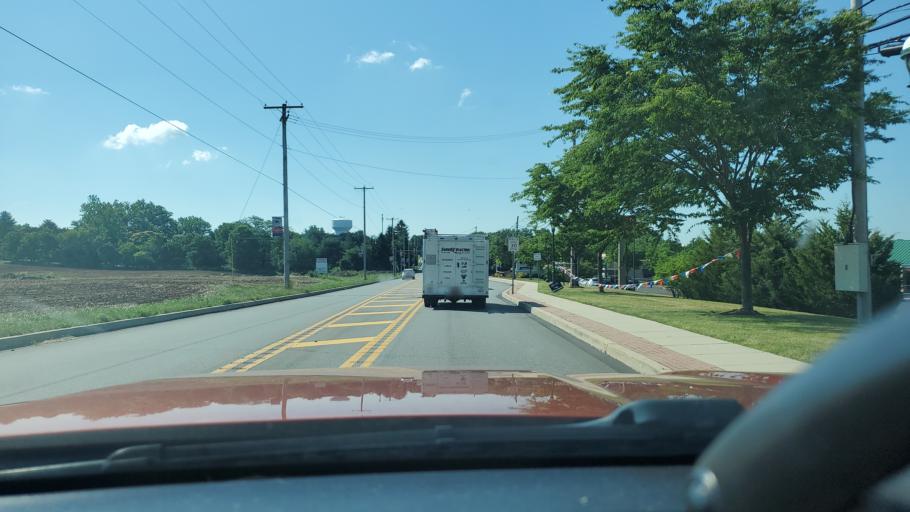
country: US
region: Pennsylvania
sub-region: Montgomery County
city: East Greenville
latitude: 40.4137
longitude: -75.5085
